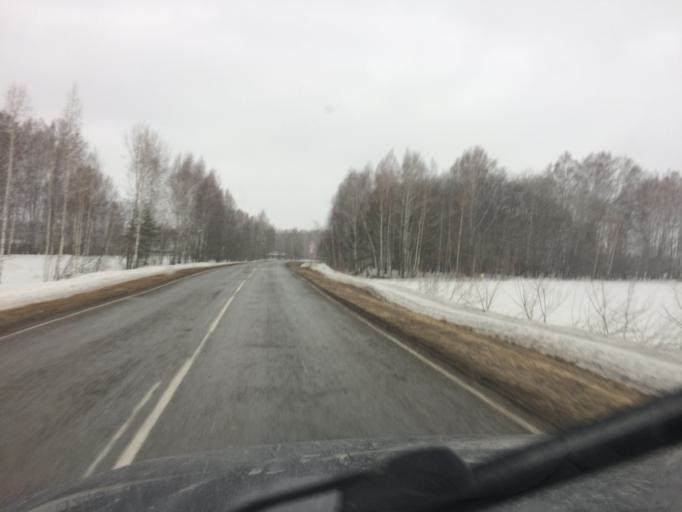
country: RU
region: Novosibirsk
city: Tashara
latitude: 55.4579
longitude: 83.3575
